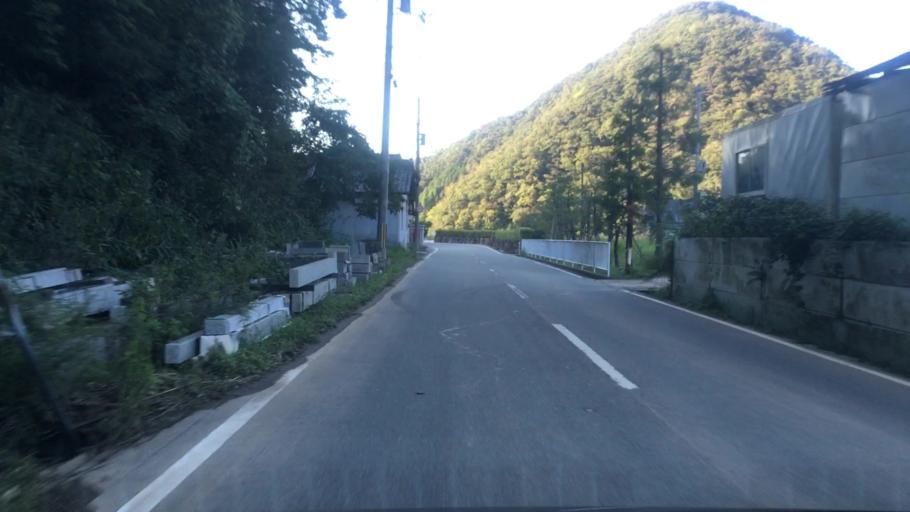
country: JP
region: Hyogo
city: Toyooka
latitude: 35.6148
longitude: 134.8268
